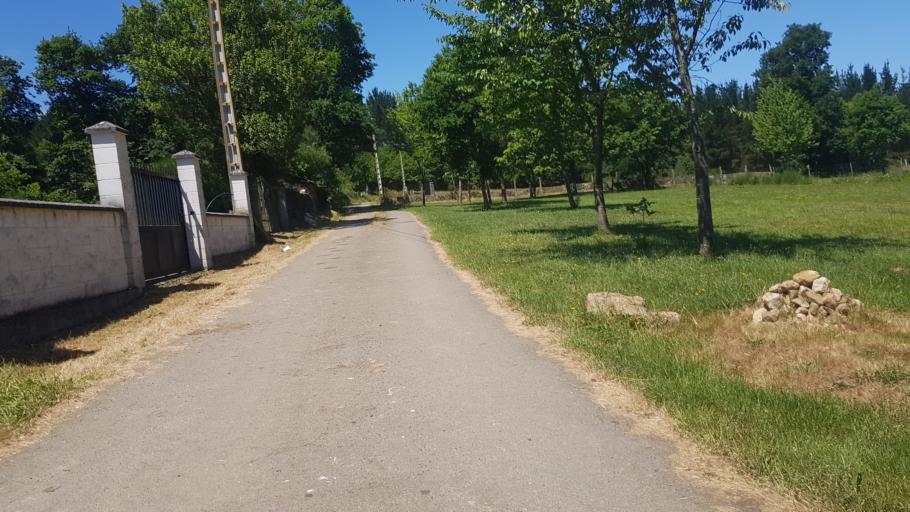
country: ES
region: Galicia
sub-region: Provincia de Lugo
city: Begonte
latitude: 43.1333
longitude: -7.7687
